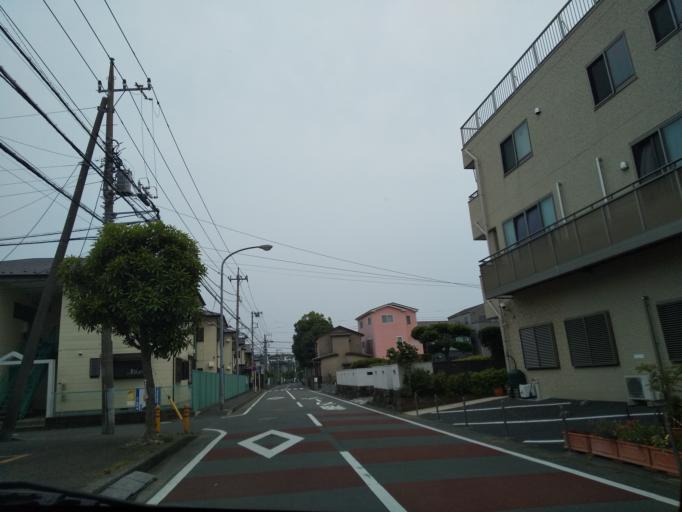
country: JP
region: Kanagawa
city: Minami-rinkan
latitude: 35.4632
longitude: 139.4270
